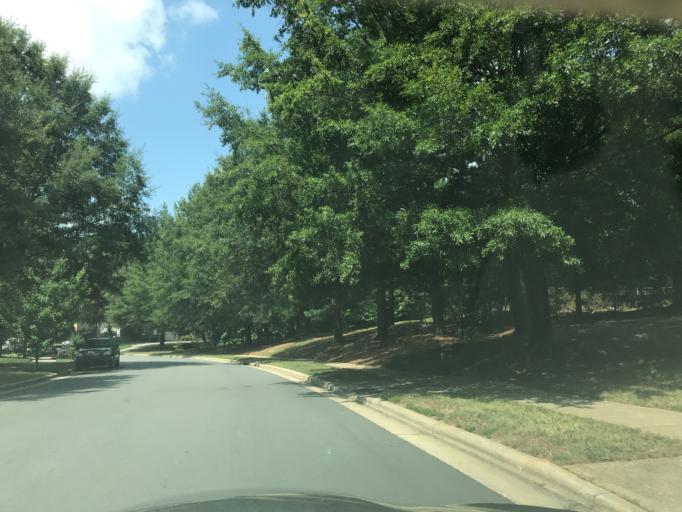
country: US
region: North Carolina
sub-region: Wake County
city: Wake Forest
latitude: 35.9106
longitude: -78.5883
